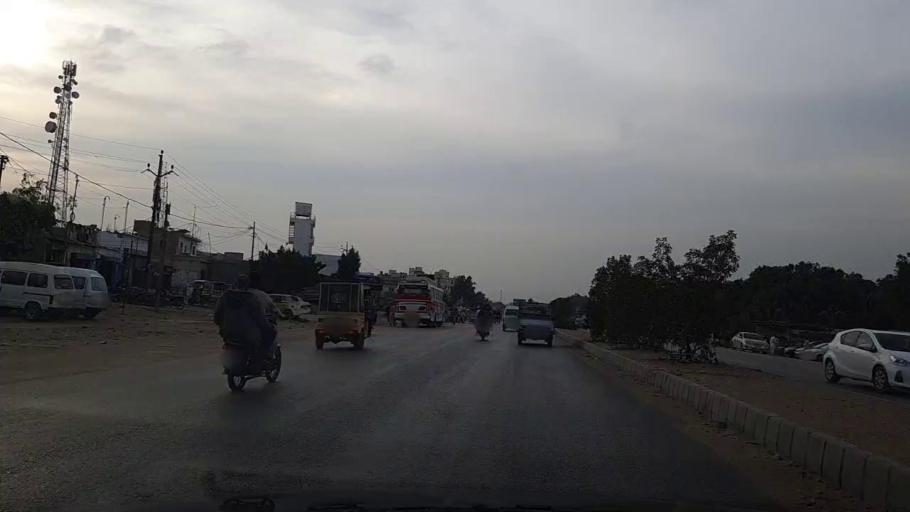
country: PK
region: Sindh
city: Malir Cantonment
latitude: 24.8597
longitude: 67.3373
